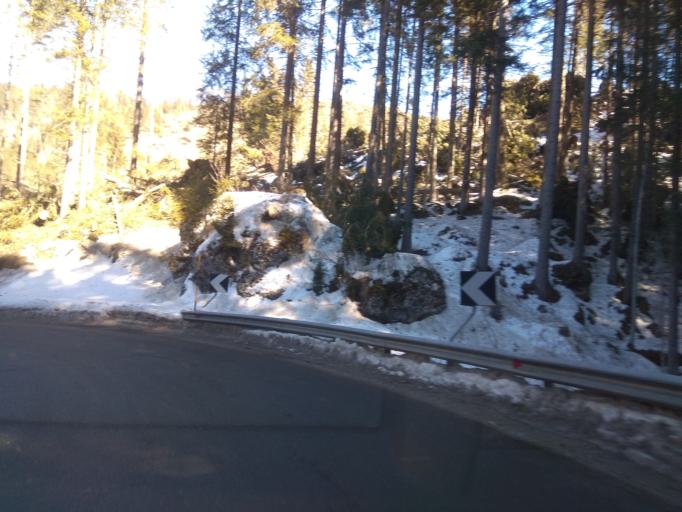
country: IT
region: Trentino-Alto Adige
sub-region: Bolzano
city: Nova Levante
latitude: 46.4149
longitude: 11.5673
